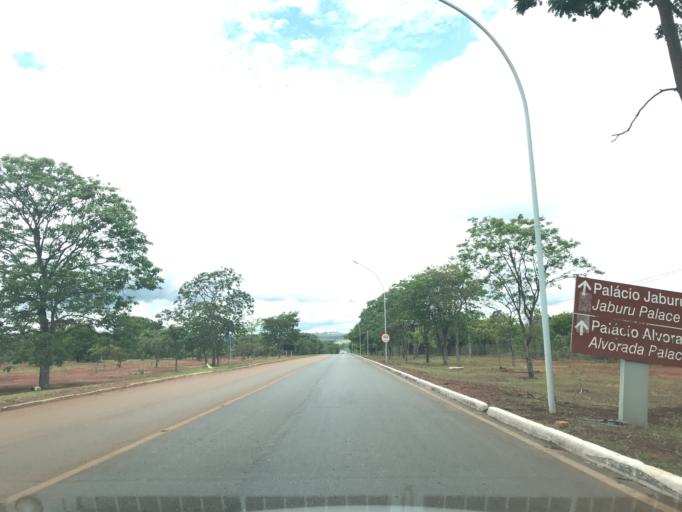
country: BR
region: Federal District
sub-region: Brasilia
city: Brasilia
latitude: -15.8006
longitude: -47.8467
